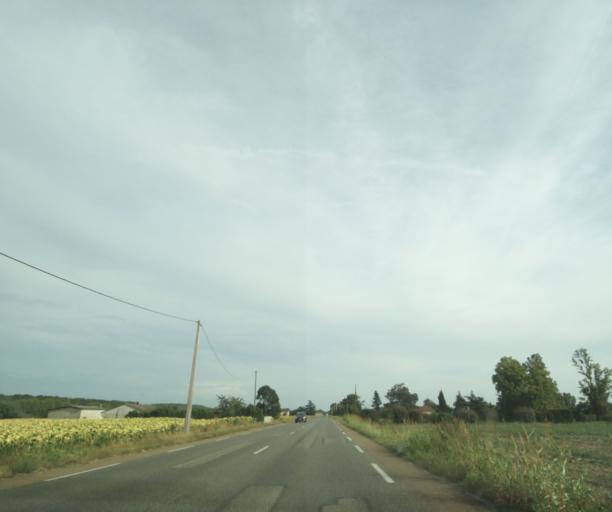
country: FR
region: Midi-Pyrenees
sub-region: Departement du Tarn-et-Garonne
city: Verdun-sur-Garonne
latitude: 43.8749
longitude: 1.2606
